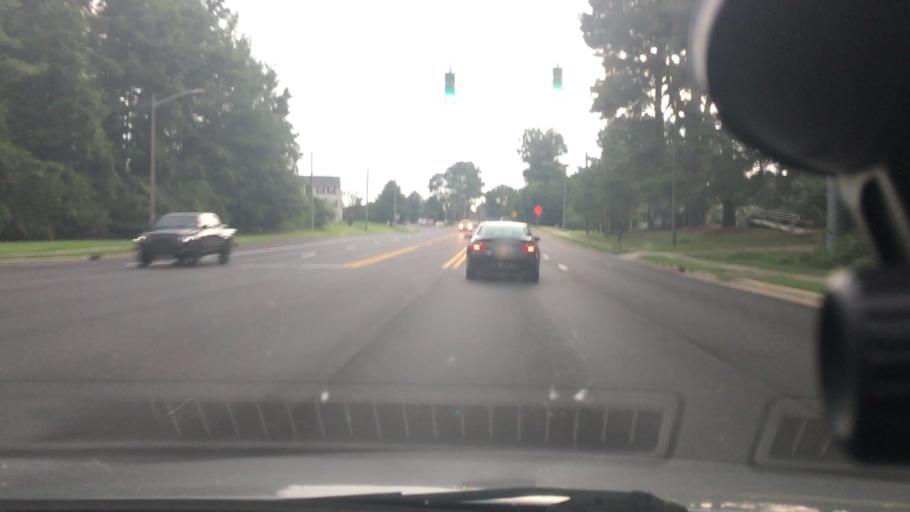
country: US
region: North Carolina
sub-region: Pitt County
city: Greenville
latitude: 35.5957
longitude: -77.3234
